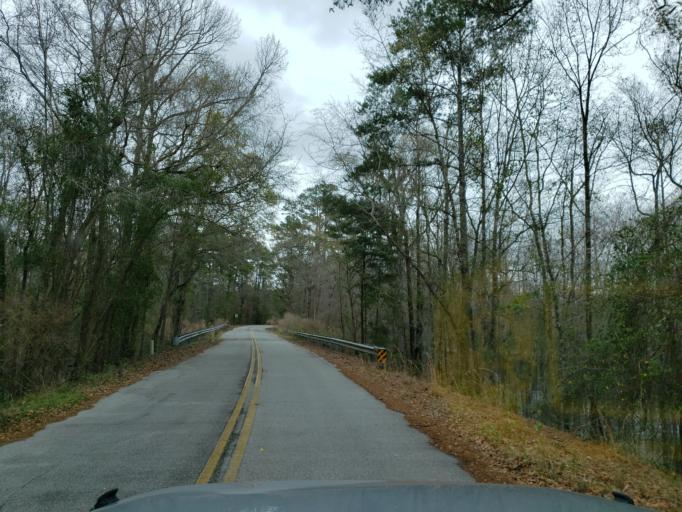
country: US
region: Georgia
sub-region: Chatham County
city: Bloomingdale
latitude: 32.0841
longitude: -81.3786
